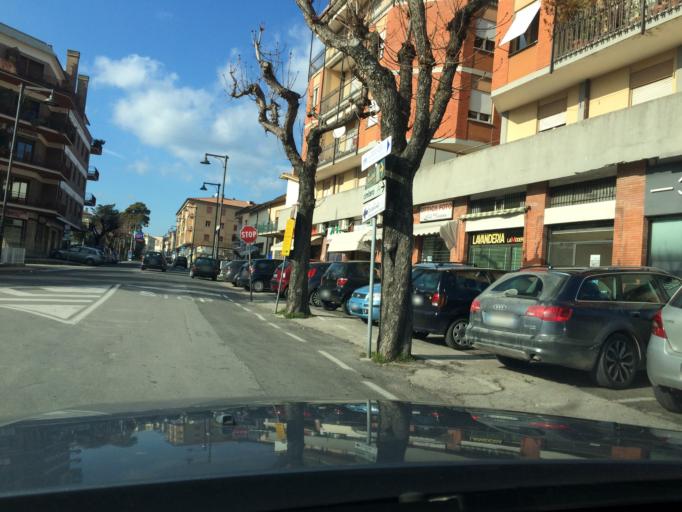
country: IT
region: Umbria
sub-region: Provincia di Terni
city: Amelia
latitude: 42.5516
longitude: 12.4205
